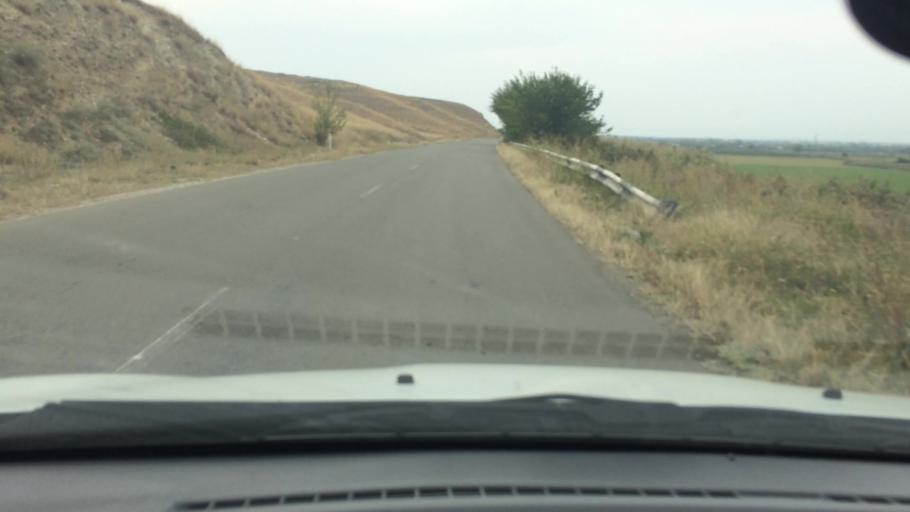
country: AM
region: Tavush
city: Berdavan
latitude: 41.3396
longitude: 44.9977
